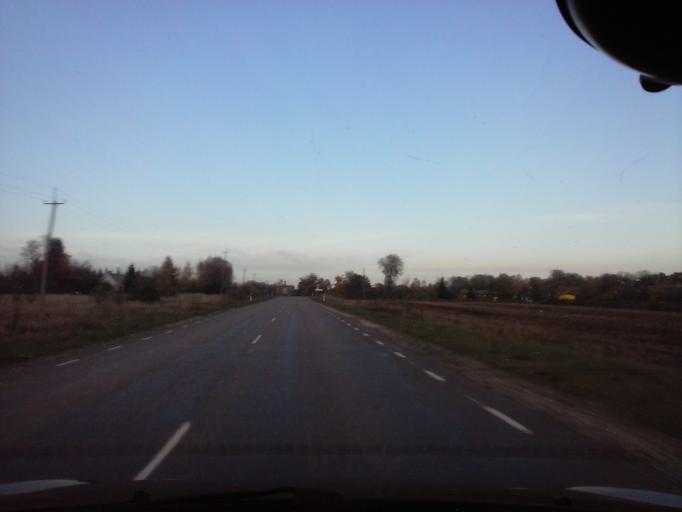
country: EE
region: Harju
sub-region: Nissi vald
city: Turba
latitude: 58.9142
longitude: 24.1548
